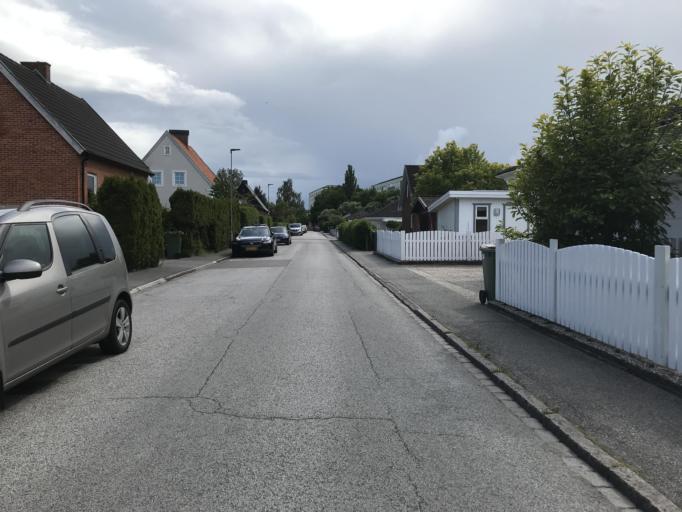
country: SE
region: Skane
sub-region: Malmo
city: Malmoe
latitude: 55.5696
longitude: 13.0283
